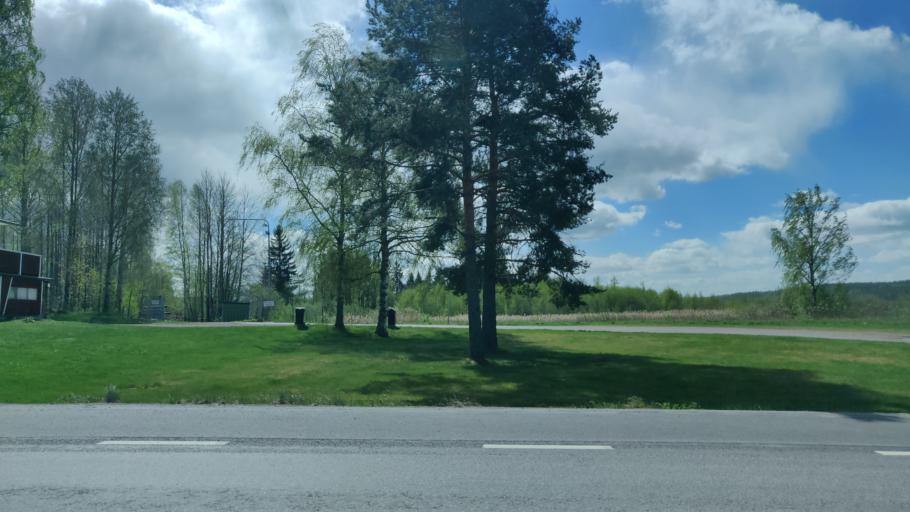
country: SE
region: Vaermland
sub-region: Karlstads Kommun
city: Molkom
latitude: 59.5976
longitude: 13.7233
